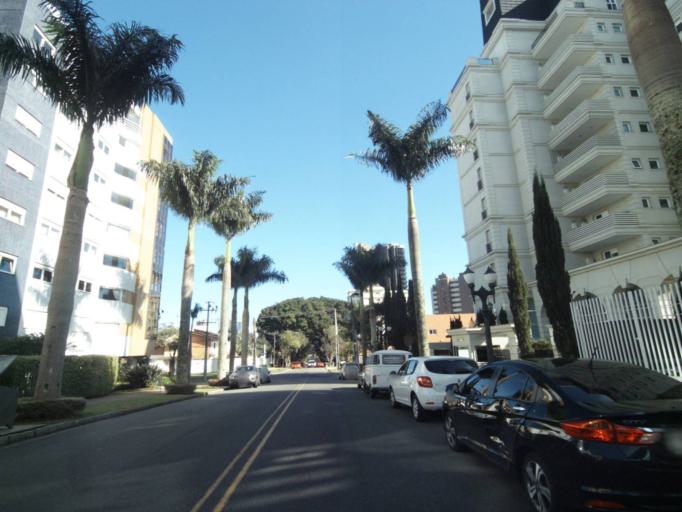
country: BR
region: Parana
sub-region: Curitiba
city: Curitiba
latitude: -25.4113
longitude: -49.2443
